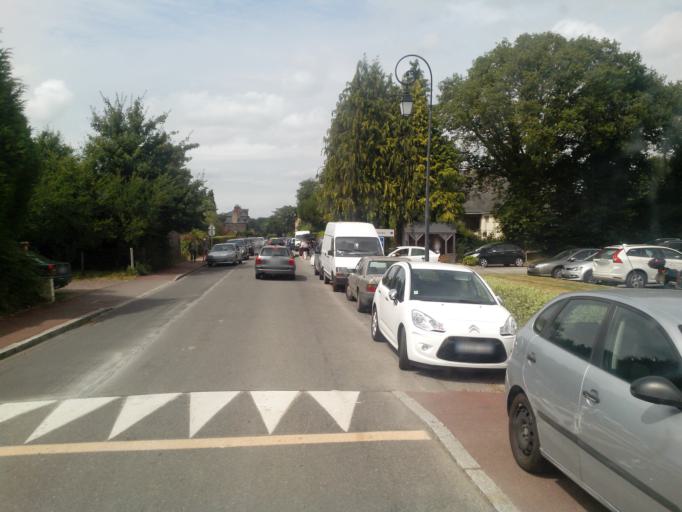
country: FR
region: Brittany
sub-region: Departement d'Ille-et-Vilaine
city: Paimpont
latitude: 48.0169
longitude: -2.1698
